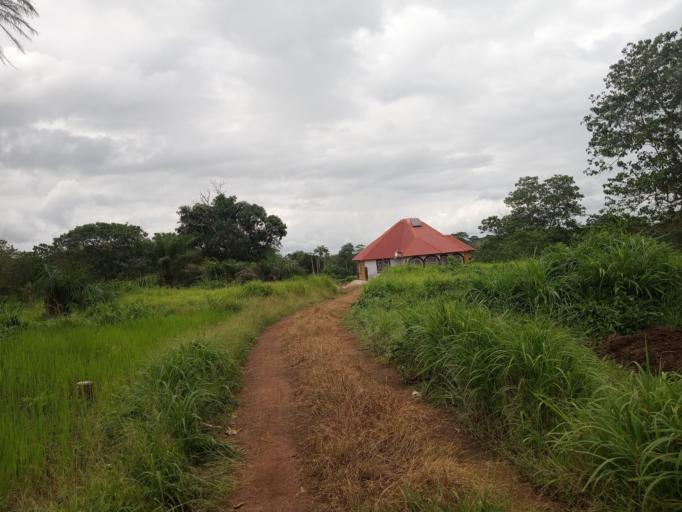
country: SL
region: Northern Province
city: Kamakwie
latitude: 9.4995
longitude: -12.2514
